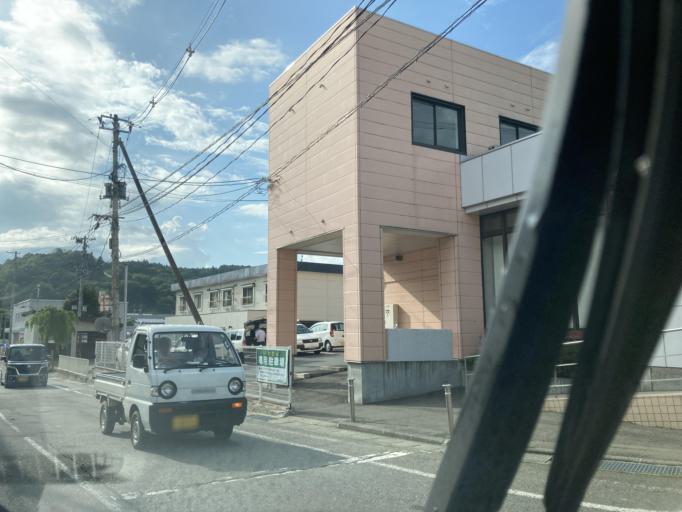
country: JP
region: Iwate
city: Ichinohe
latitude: 39.9711
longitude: 141.2232
